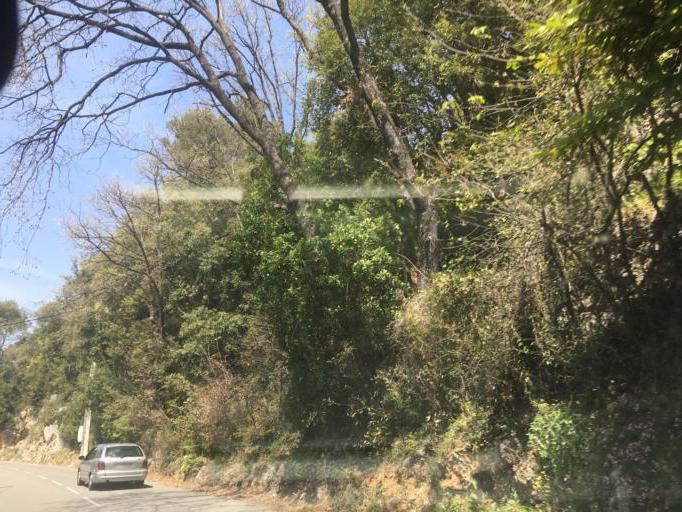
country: FR
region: Provence-Alpes-Cote d'Azur
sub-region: Departement des Alpes-Maritimes
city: Saint-Martin-du-Var
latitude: 43.8326
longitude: 7.2082
